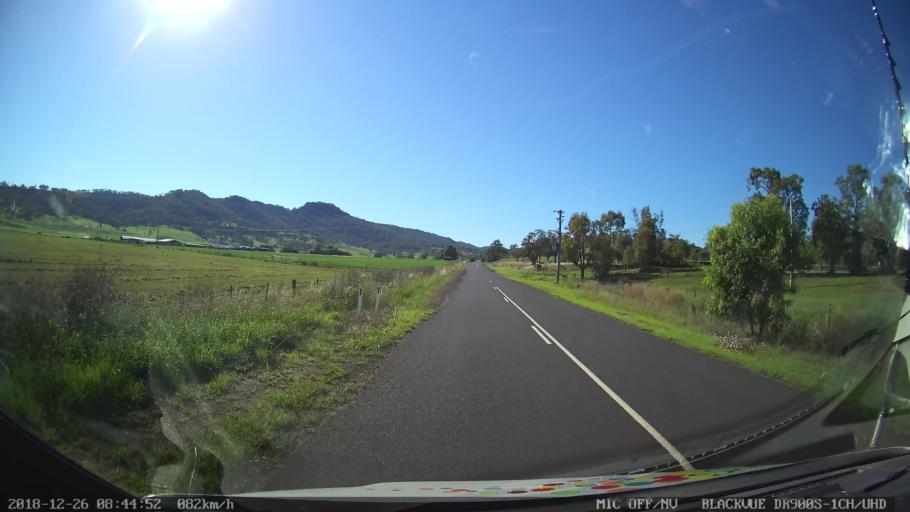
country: AU
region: New South Wales
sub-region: Mid-Western Regional
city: Kandos
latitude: -32.5197
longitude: 150.0819
